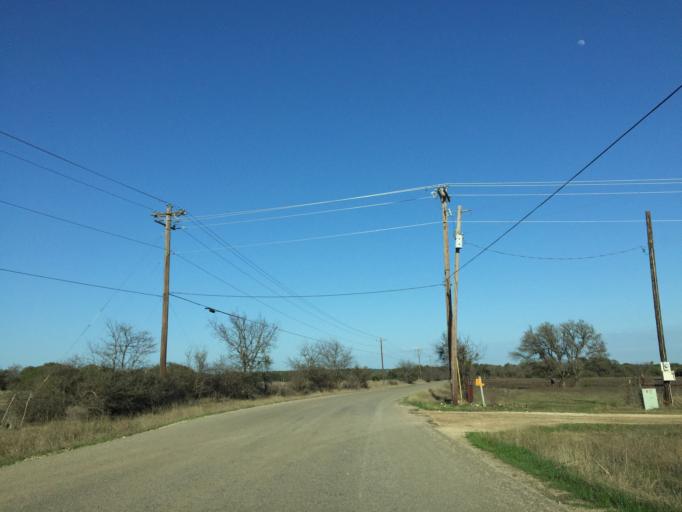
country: US
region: Texas
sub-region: Williamson County
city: Florence
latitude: 30.7729
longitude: -97.8160
